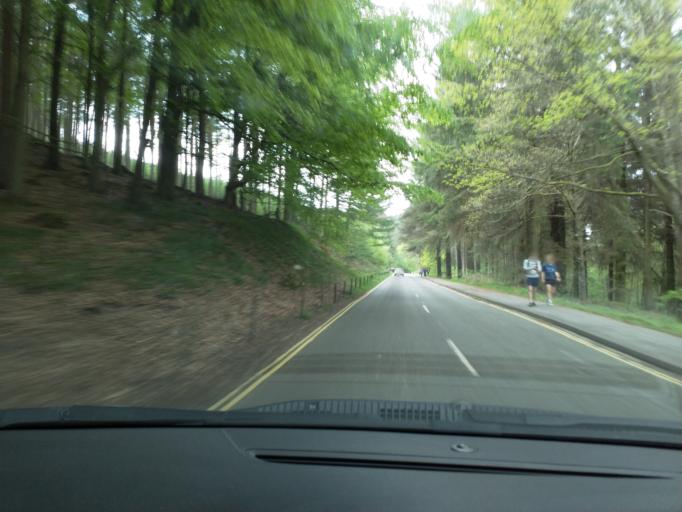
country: GB
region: England
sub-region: Derbyshire
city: Hope Valley
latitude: 53.3948
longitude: -1.7374
